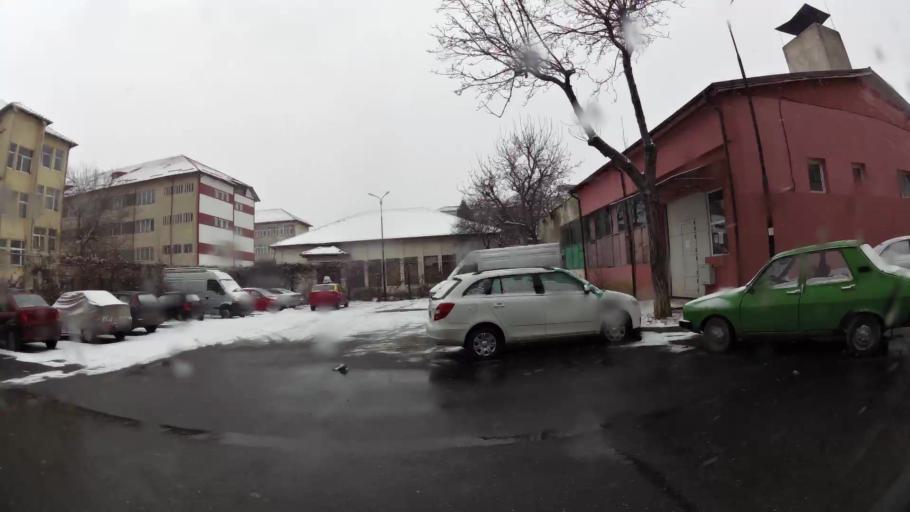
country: RO
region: Dambovita
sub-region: Municipiul Targoviste
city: Targoviste
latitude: 44.9297
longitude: 25.4487
